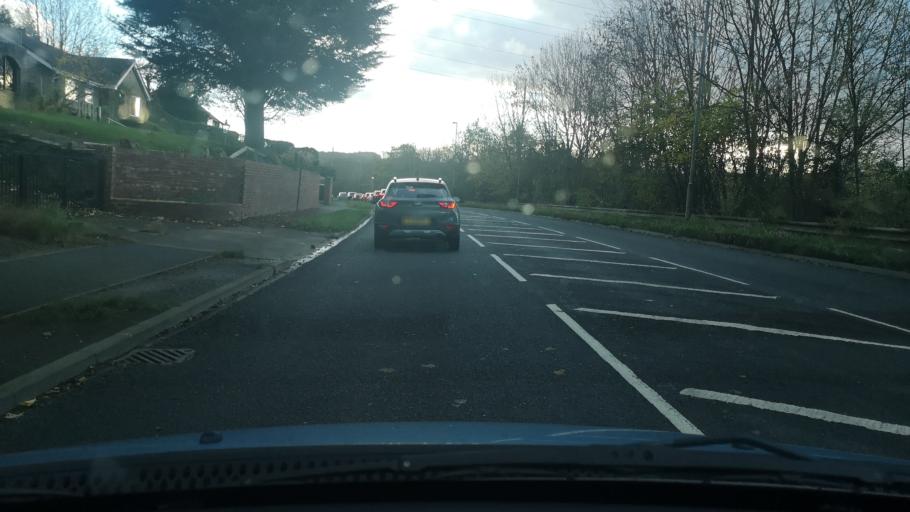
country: GB
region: England
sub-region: City and Borough of Wakefield
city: Crigglestone
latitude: 53.6454
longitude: -1.5454
